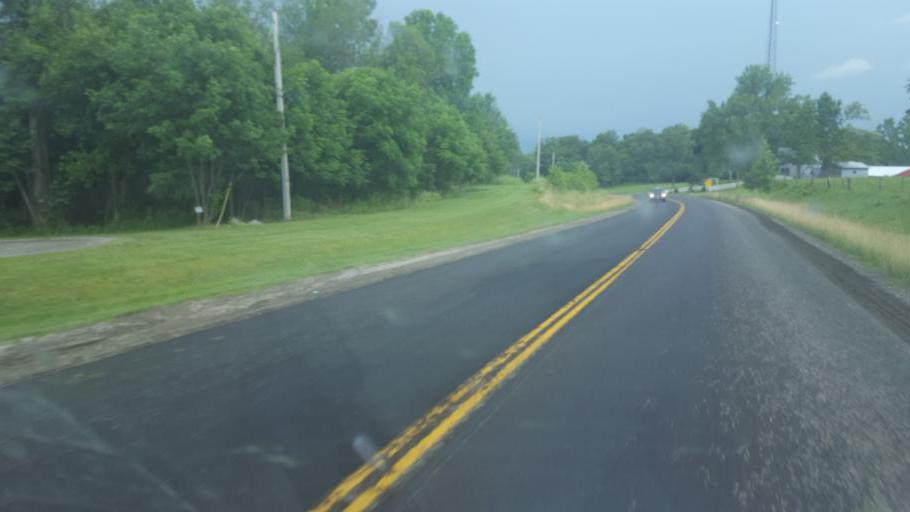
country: US
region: Ohio
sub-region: Knox County
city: Fredericktown
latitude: 40.5404
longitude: -82.6631
